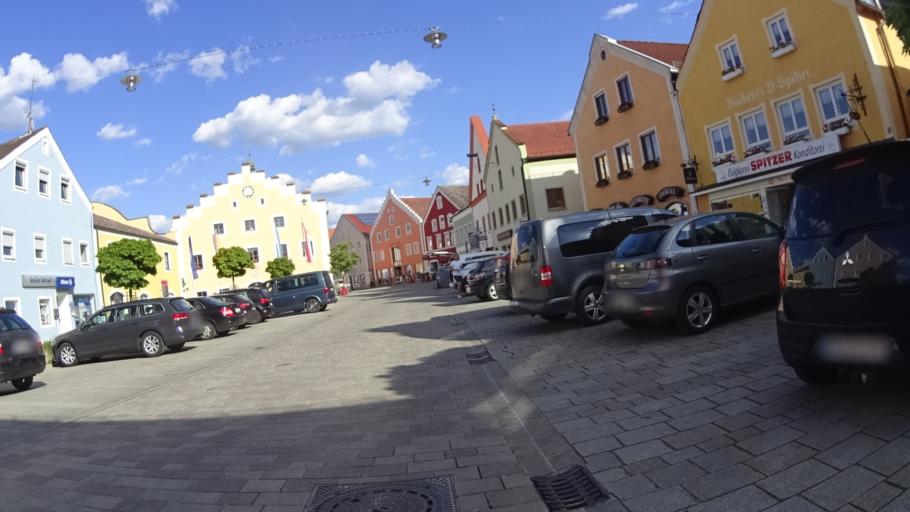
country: DE
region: Bavaria
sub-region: Upper Palatinate
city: Dietfurt
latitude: 49.0353
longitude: 11.5868
